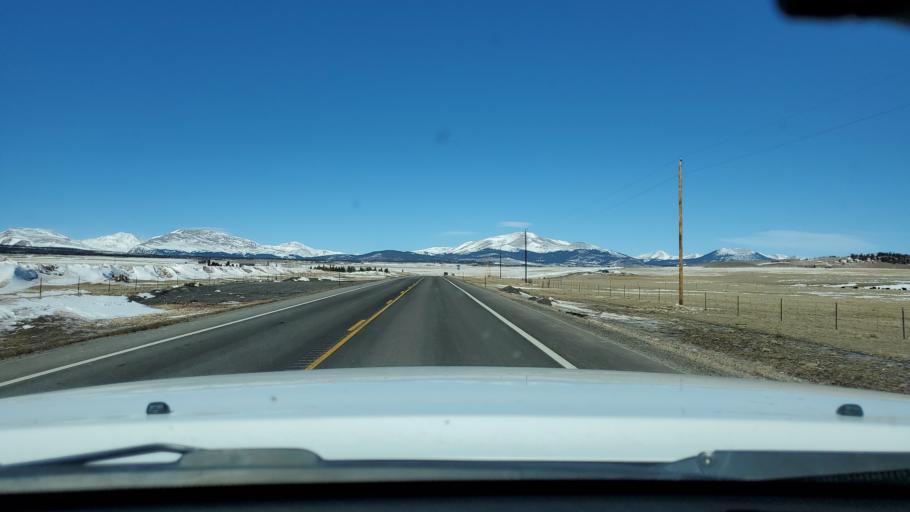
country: US
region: Colorado
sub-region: Park County
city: Fairplay
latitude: 39.1646
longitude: -106.0012
